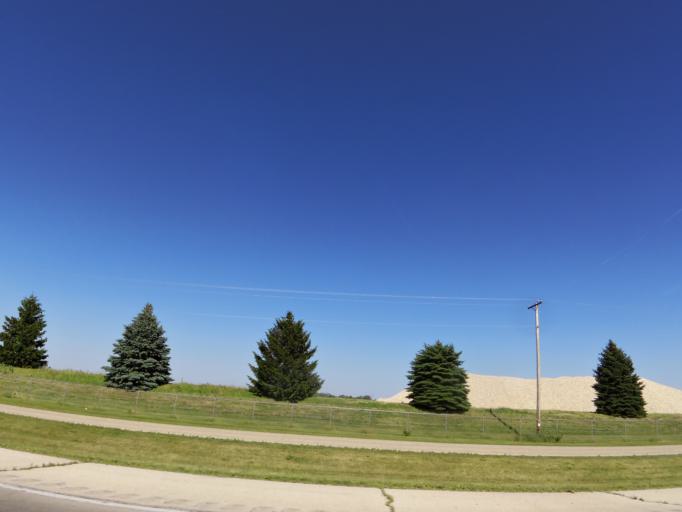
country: US
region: Illinois
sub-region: Winnebago County
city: South Beloit
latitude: 42.4761
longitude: -89.0194
